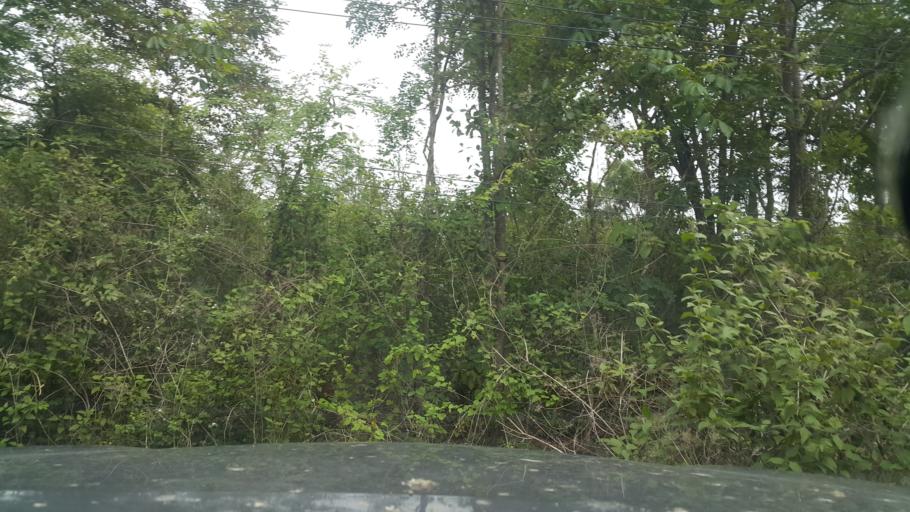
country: TH
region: Chiang Mai
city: Hang Dong
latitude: 18.6965
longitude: 98.8600
